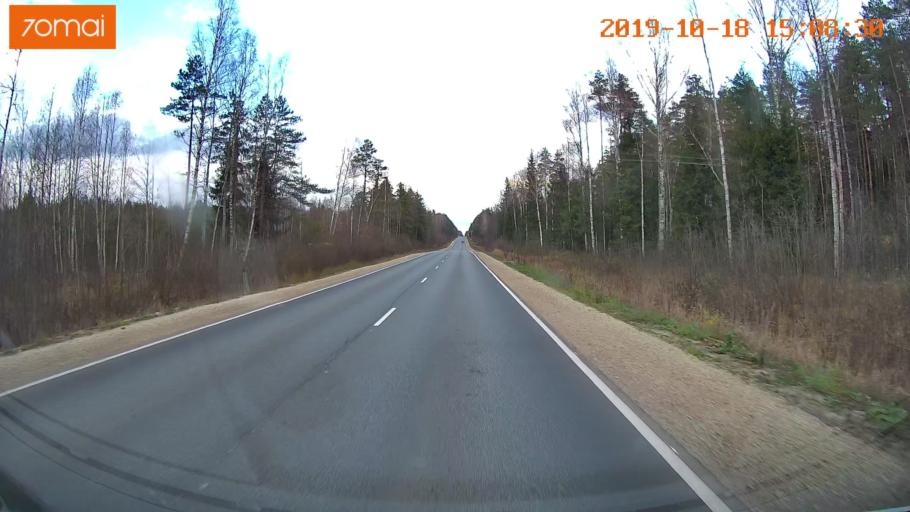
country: RU
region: Vladimir
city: Gus'-Khrustal'nyy
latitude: 55.5532
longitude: 40.6112
